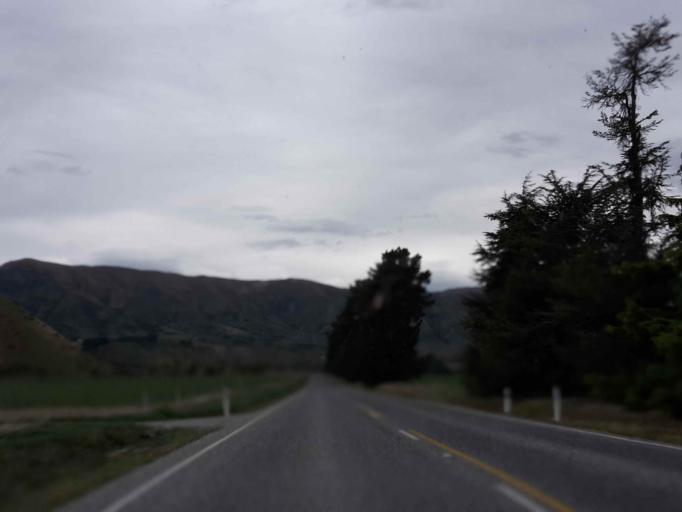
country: NZ
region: Otago
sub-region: Queenstown-Lakes District
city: Wanaka
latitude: -44.7334
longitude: 169.2977
